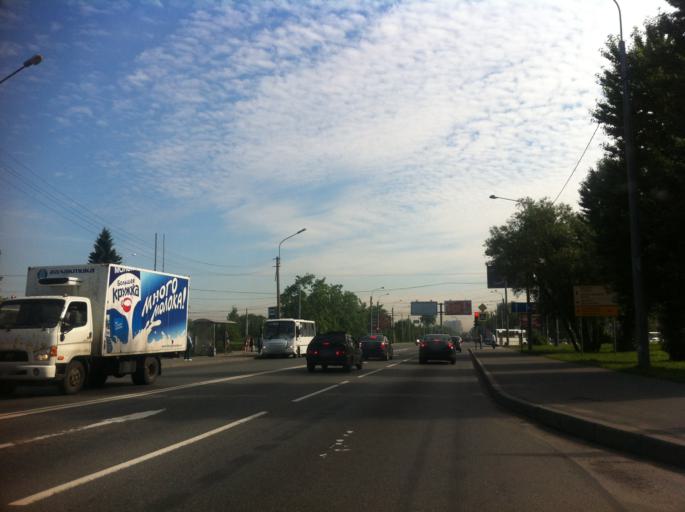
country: RU
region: St.-Petersburg
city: Uritsk
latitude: 59.8322
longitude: 30.1936
